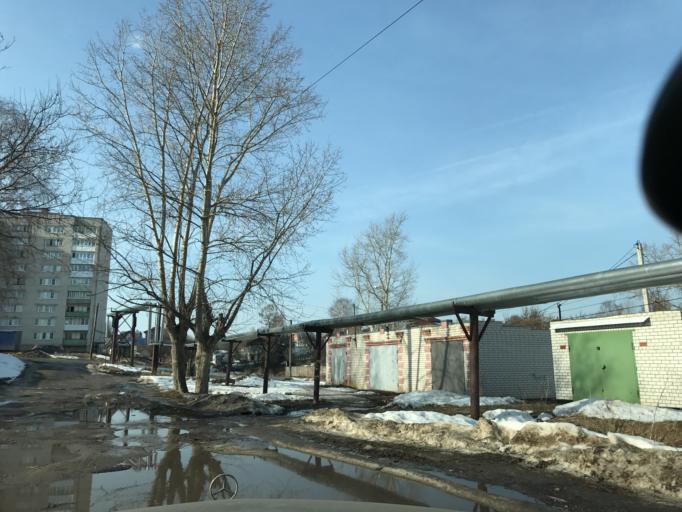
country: RU
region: Nizjnij Novgorod
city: Taremskoye
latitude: 55.9556
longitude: 43.0544
